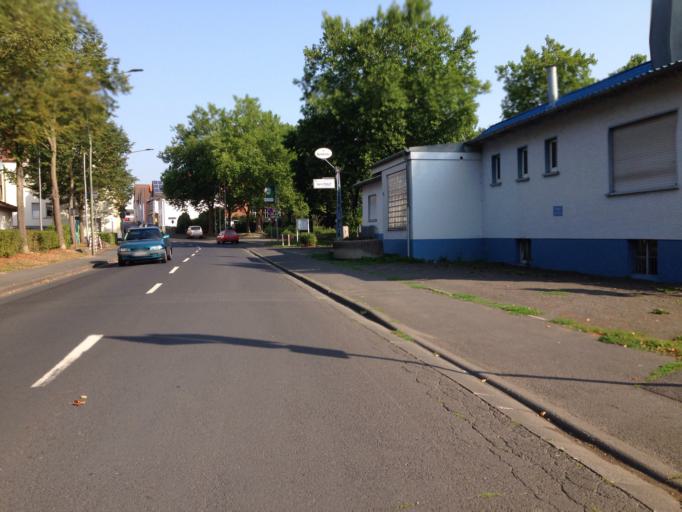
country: DE
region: Hesse
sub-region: Regierungsbezirk Giessen
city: Giessen
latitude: 50.6011
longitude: 8.7071
